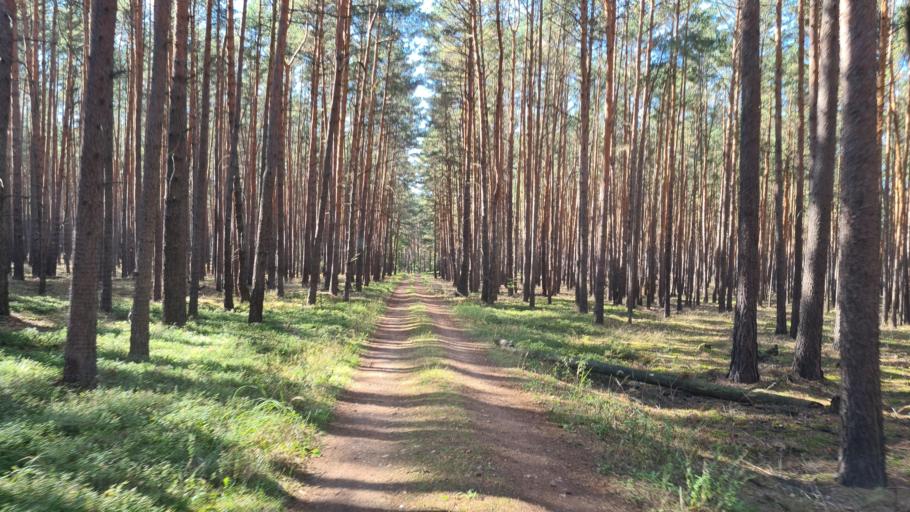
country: DE
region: Brandenburg
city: Lebusa
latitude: 51.8375
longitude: 13.4880
